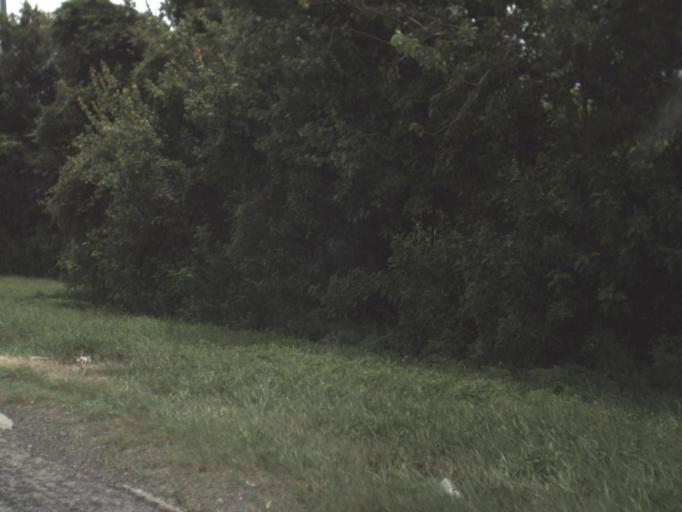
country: US
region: Florida
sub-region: Hillsborough County
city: East Lake-Orient Park
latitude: 27.9961
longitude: -82.3695
